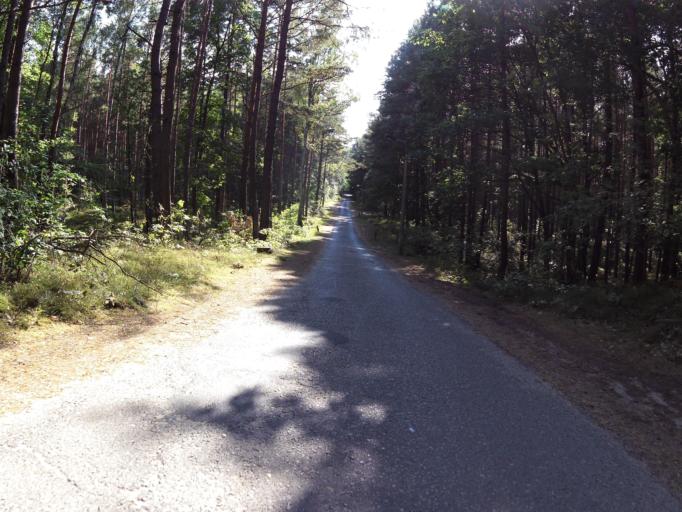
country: DE
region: Mecklenburg-Vorpommern
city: Seebad Heringsdorf
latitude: 53.9329
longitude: 14.2028
